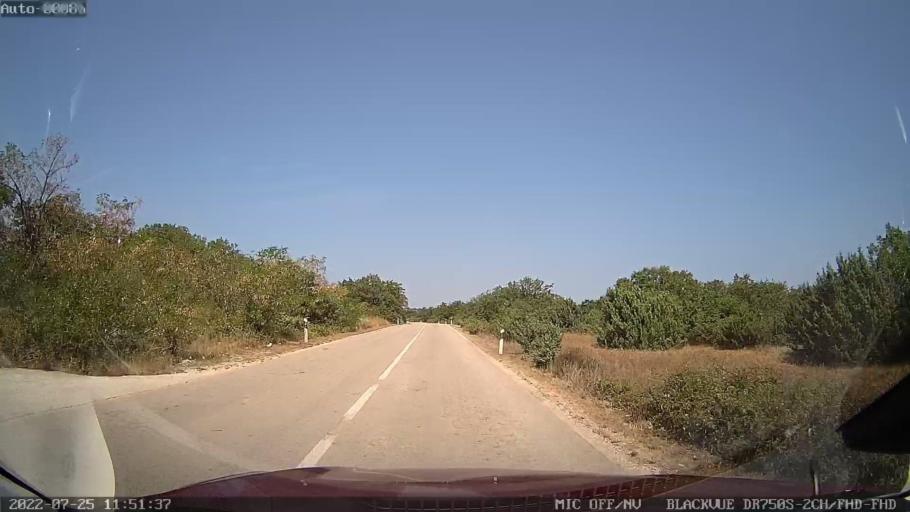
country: HR
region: Zadarska
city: Vrsi
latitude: 44.2405
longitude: 15.2509
